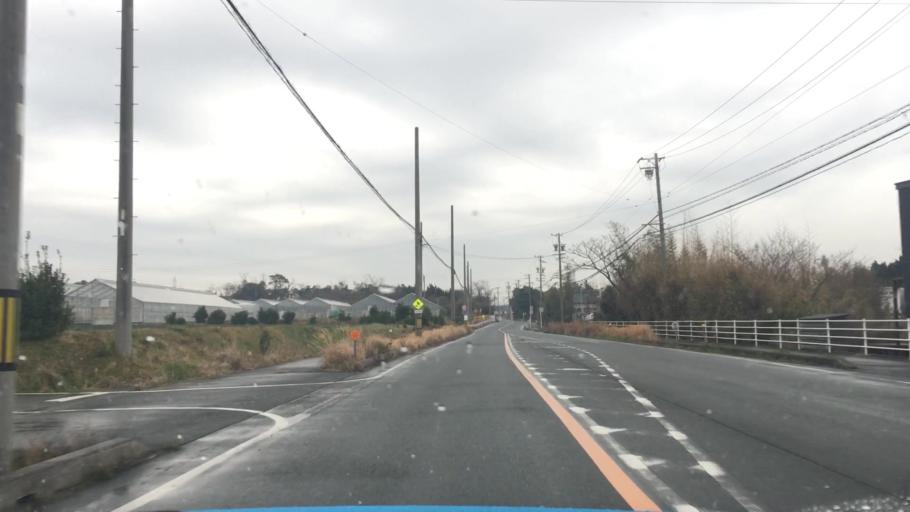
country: JP
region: Aichi
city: Toyohashi
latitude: 34.6898
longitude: 137.3904
